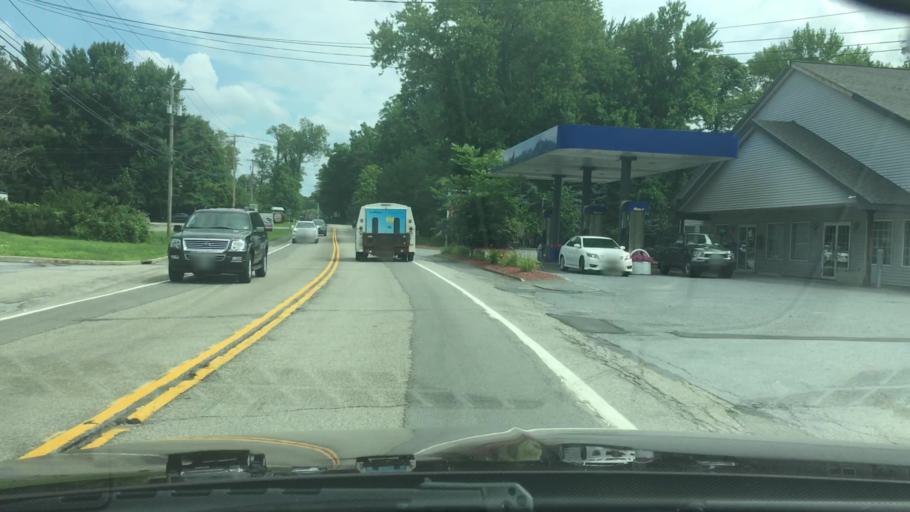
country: US
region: New York
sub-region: Dutchess County
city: Hillside Lake
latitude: 41.5552
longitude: -73.7830
